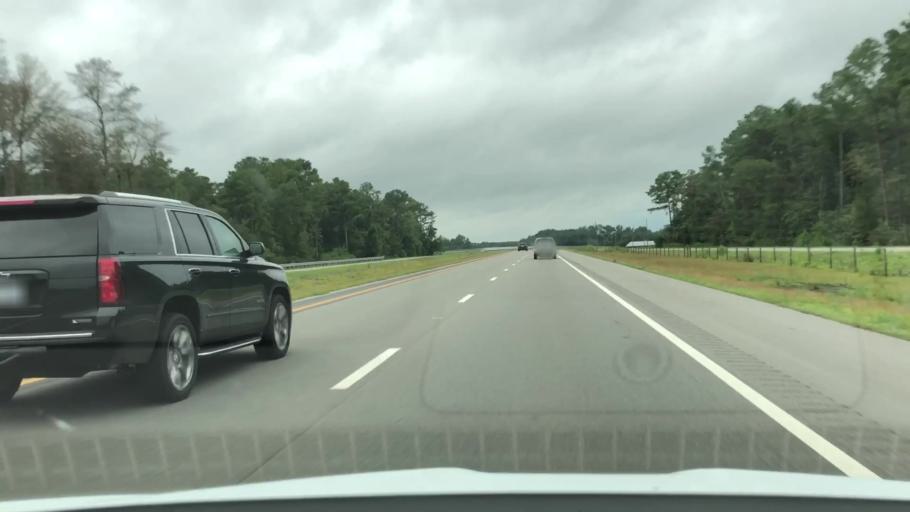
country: US
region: North Carolina
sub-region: Wayne County
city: Elroy
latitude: 35.3502
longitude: -77.8473
